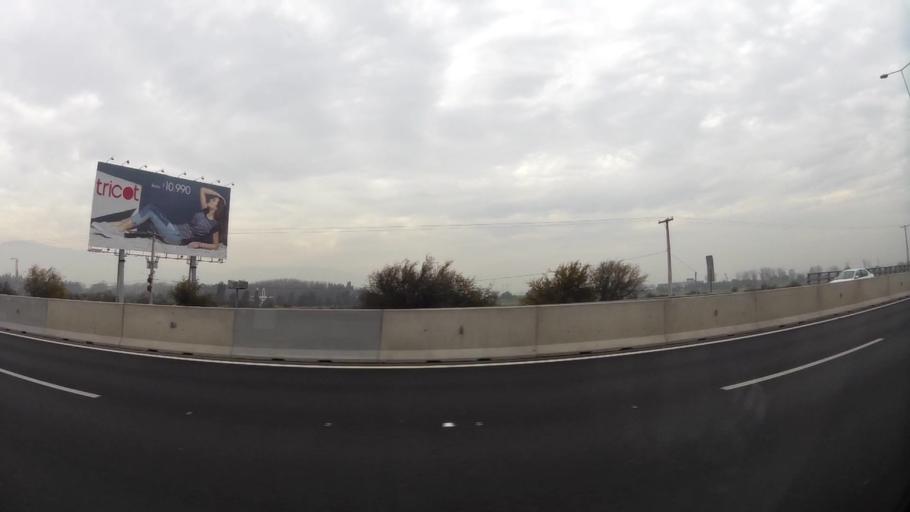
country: CL
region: Santiago Metropolitan
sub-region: Provincia de Santiago
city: Lo Prado
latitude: -33.4170
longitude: -70.7893
